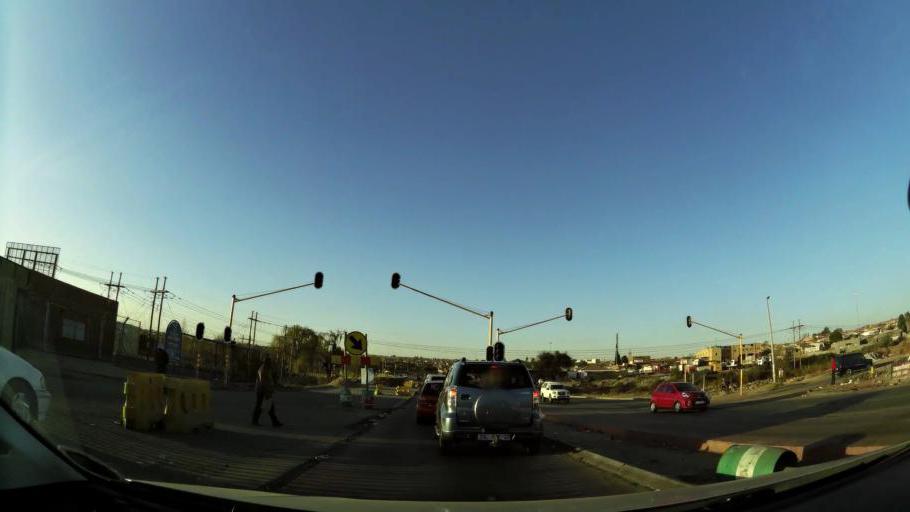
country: ZA
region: Gauteng
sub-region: Ekurhuleni Metropolitan Municipality
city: Tembisa
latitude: -26.0181
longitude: 28.2018
